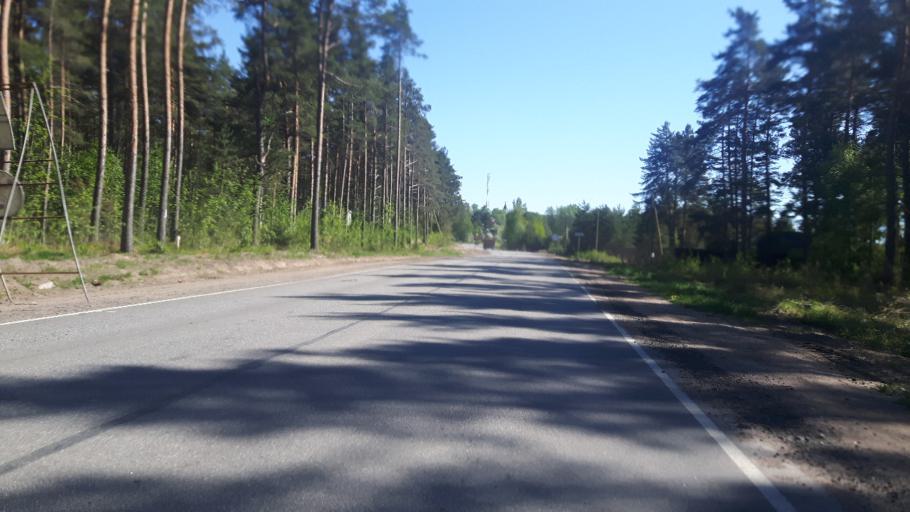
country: RU
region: Leningrad
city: Sosnovyy Bor
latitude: 60.2238
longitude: 29.0073
